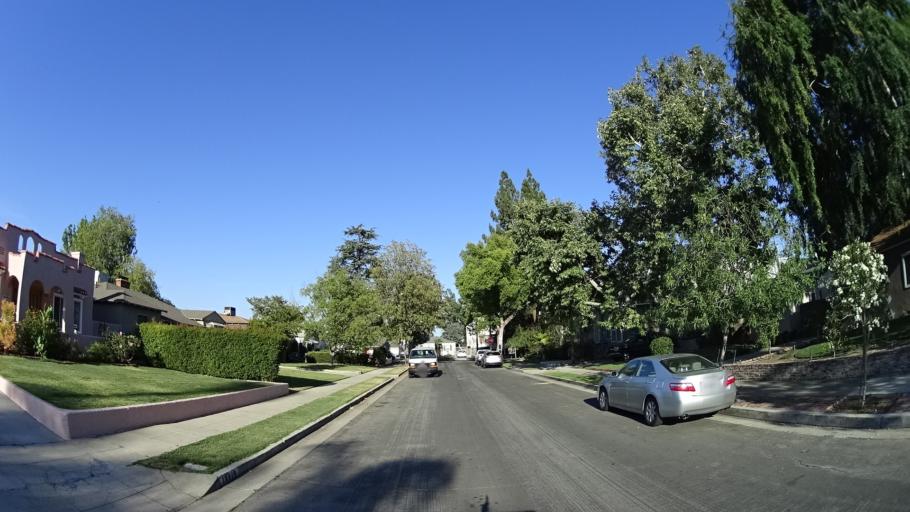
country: US
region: California
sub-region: Los Angeles County
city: North Hollywood
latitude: 34.1590
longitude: -118.3667
